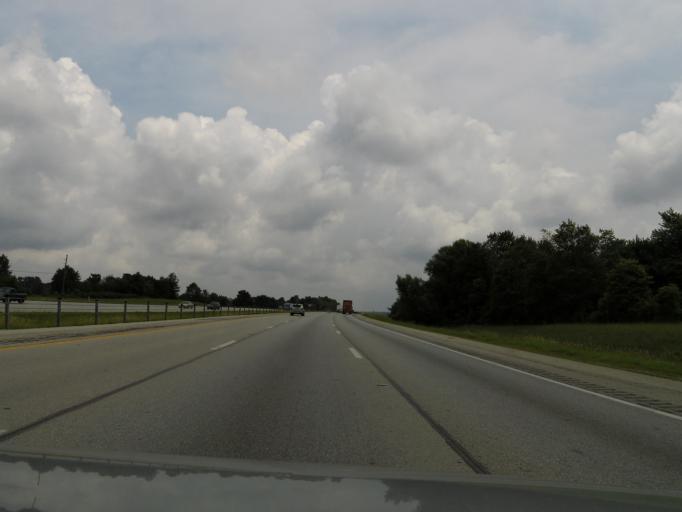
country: US
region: Kentucky
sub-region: Hardin County
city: Elizabethtown
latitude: 37.7292
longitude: -85.8184
